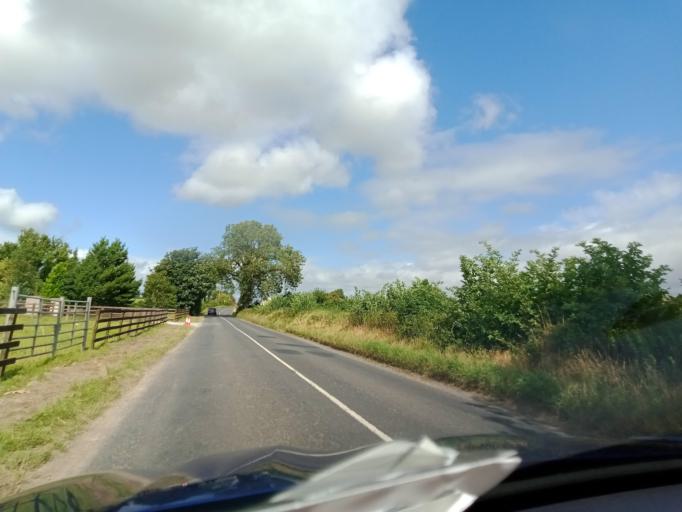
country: IE
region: Leinster
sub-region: Laois
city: Portlaoise
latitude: 52.9640
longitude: -7.2968
